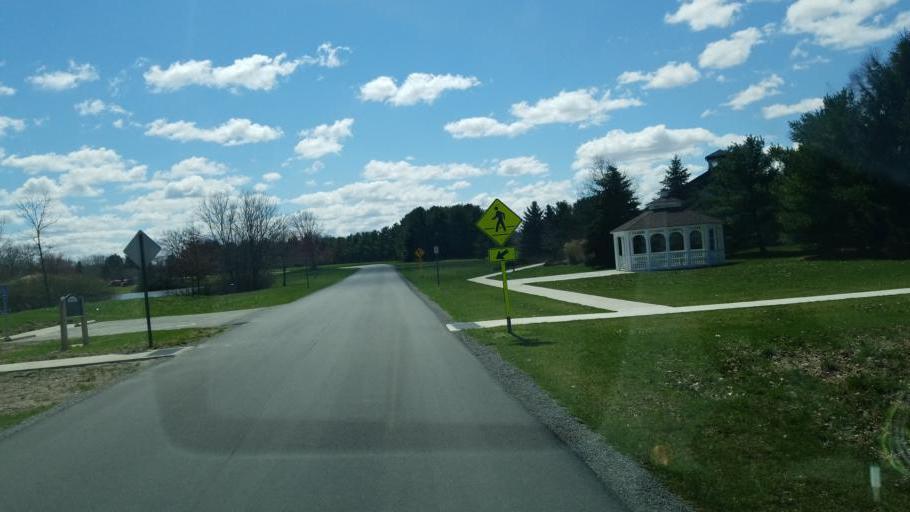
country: US
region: Ohio
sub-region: Hancock County
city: Findlay
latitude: 41.0320
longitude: -83.5608
